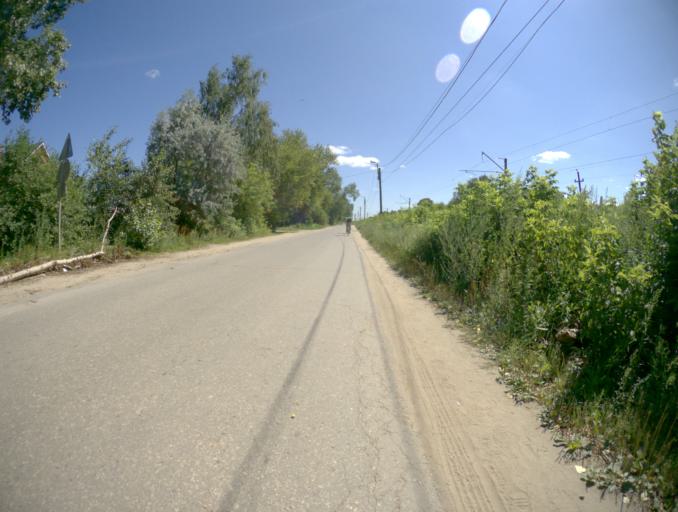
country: RU
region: Nizjnij Novgorod
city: Bor
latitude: 56.3652
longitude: 44.0627
